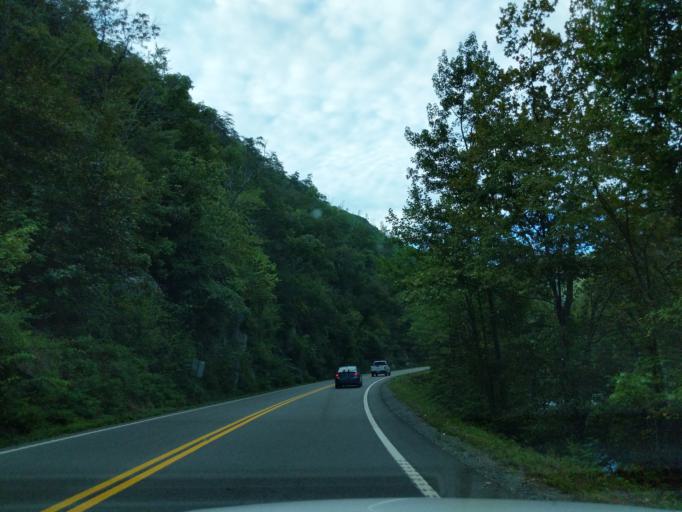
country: US
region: Tennessee
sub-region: Polk County
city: Benton
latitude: 35.0904
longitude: -84.5281
